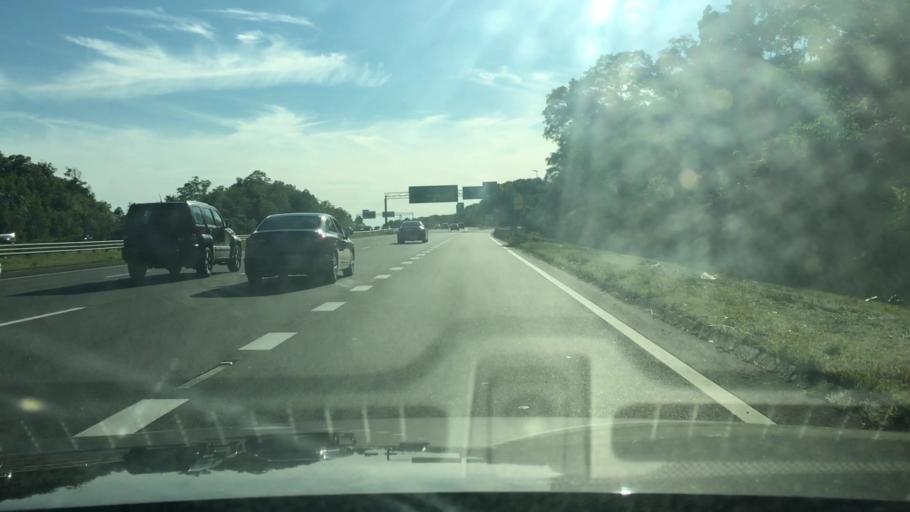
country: US
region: Massachusetts
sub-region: Essex County
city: South Peabody
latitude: 42.5260
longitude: -70.9662
